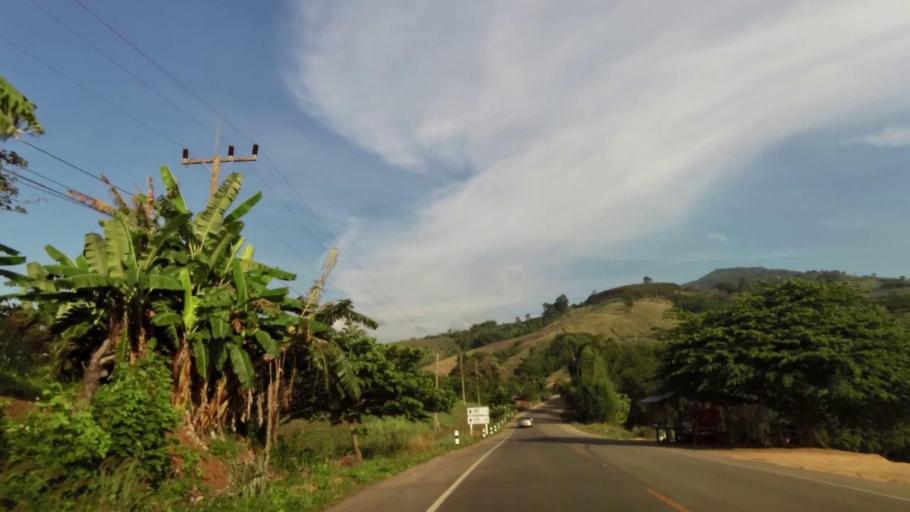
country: TH
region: Chiang Rai
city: Khun Tan
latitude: 19.8669
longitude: 100.4130
